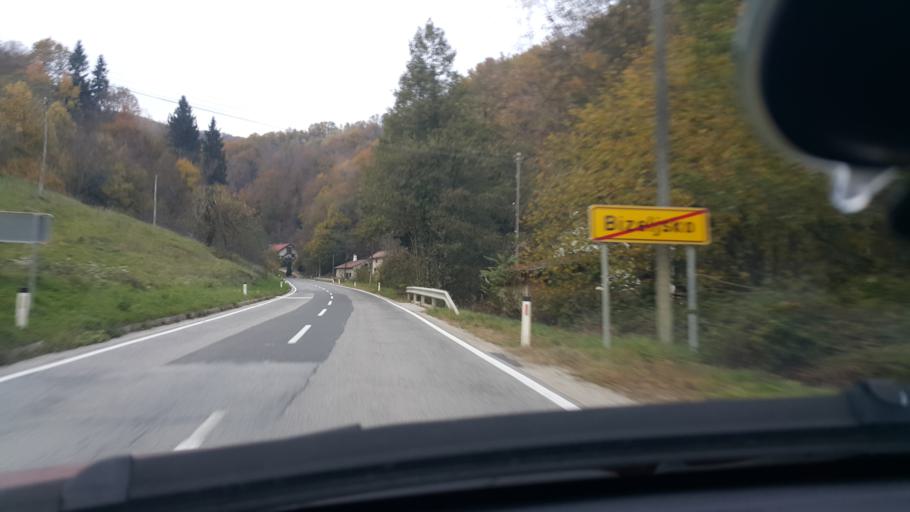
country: SI
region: Bistrica ob Sotli
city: Bistrica ob Sotli
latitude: 46.0241
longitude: 15.6890
